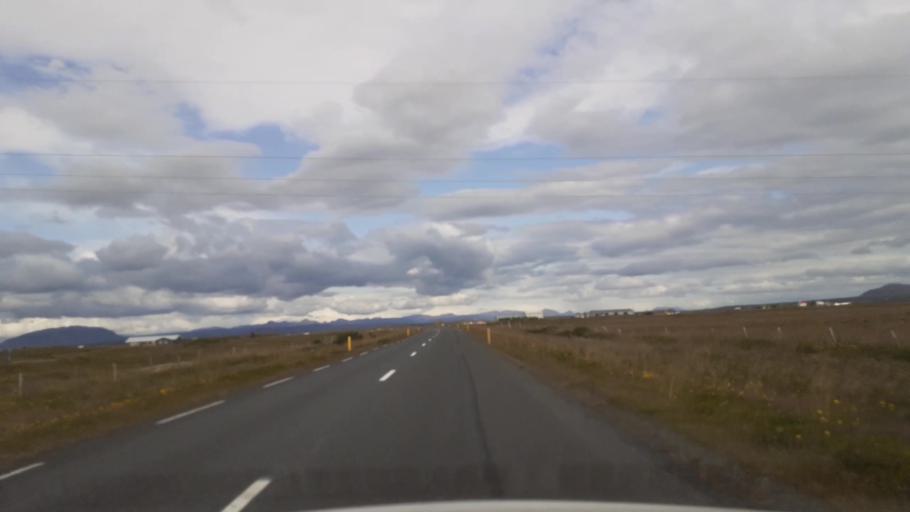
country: IS
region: South
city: Selfoss
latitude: 63.9386
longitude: -20.8395
